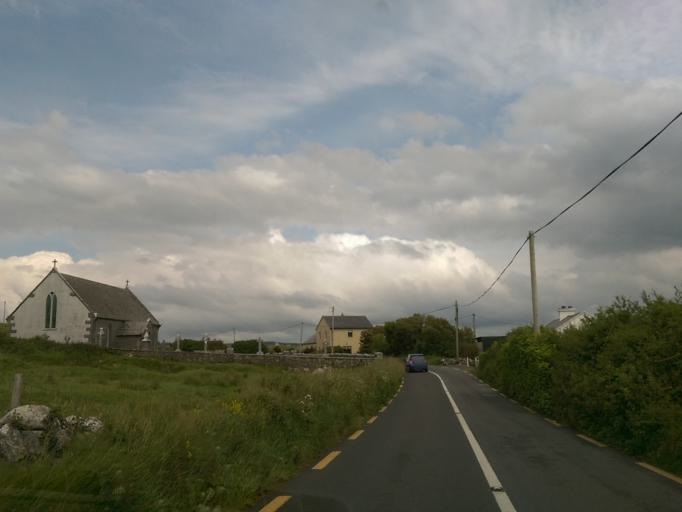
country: IE
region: Connaught
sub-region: County Galway
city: Bearna
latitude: 53.0415
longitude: -9.2608
